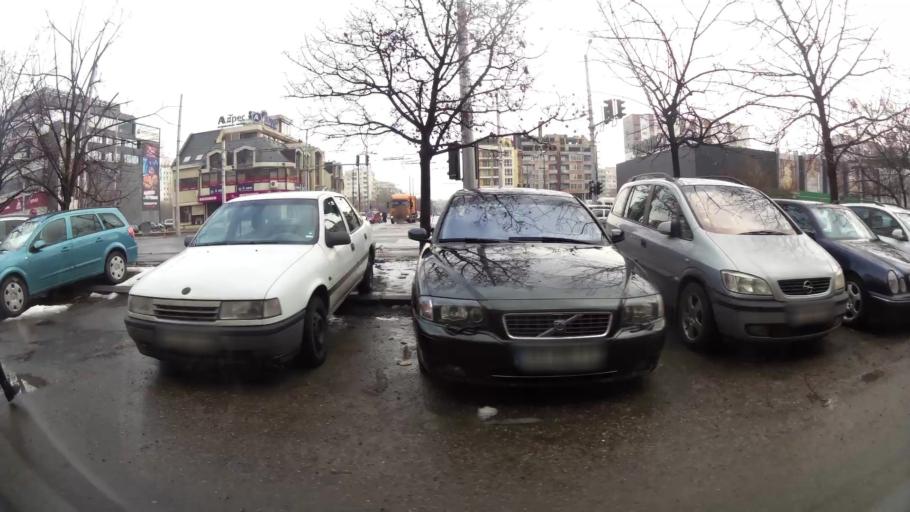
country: BG
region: Sofia-Capital
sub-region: Stolichna Obshtina
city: Sofia
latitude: 42.7131
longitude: 23.2651
